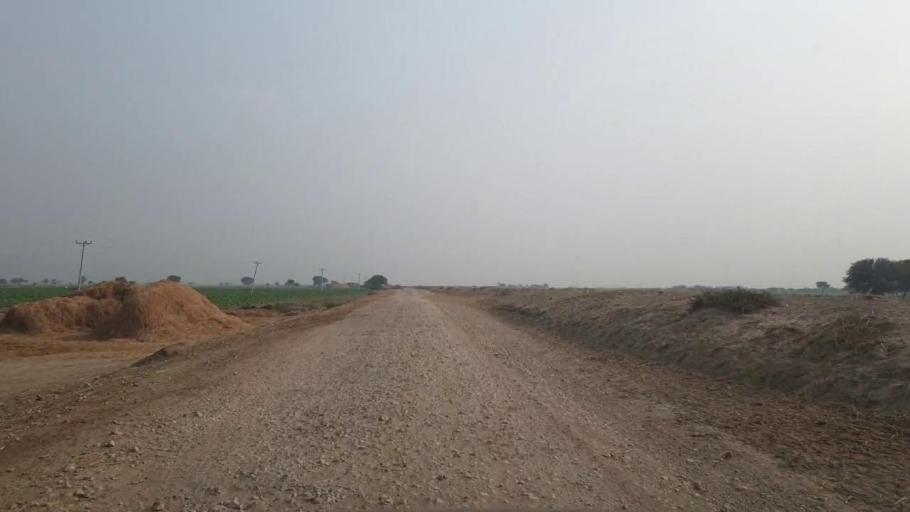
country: PK
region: Sindh
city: Mirpur Batoro
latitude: 24.5736
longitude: 68.3977
